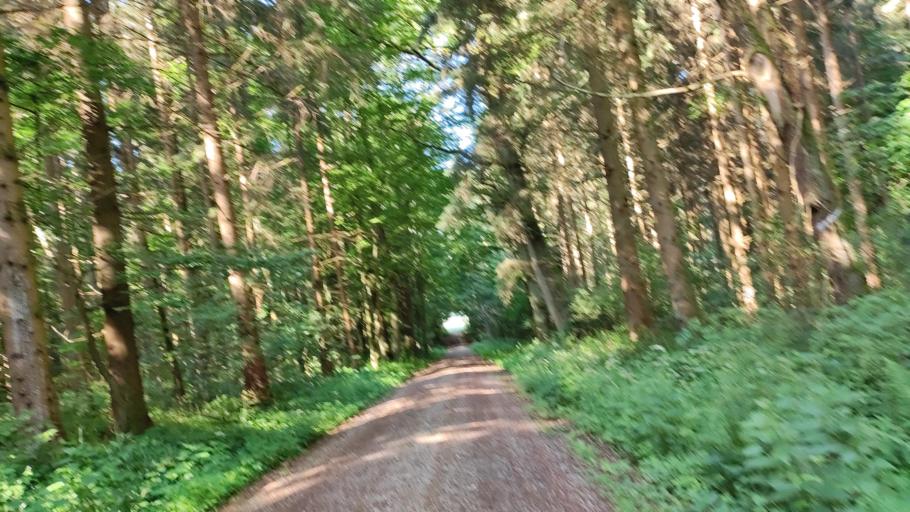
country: DE
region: Bavaria
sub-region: Swabia
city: Horgau
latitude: 48.3778
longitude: 10.7167
